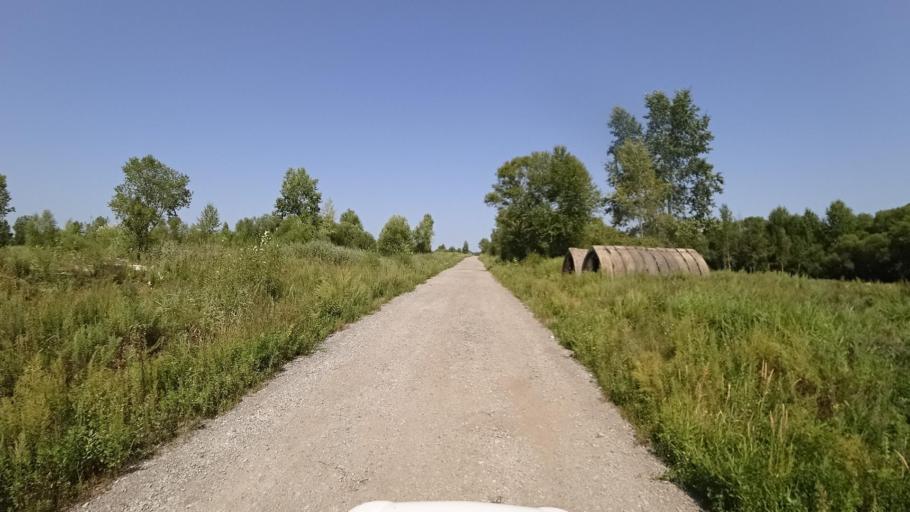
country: RU
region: Khabarovsk Krai
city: Khor
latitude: 47.9643
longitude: 135.1131
